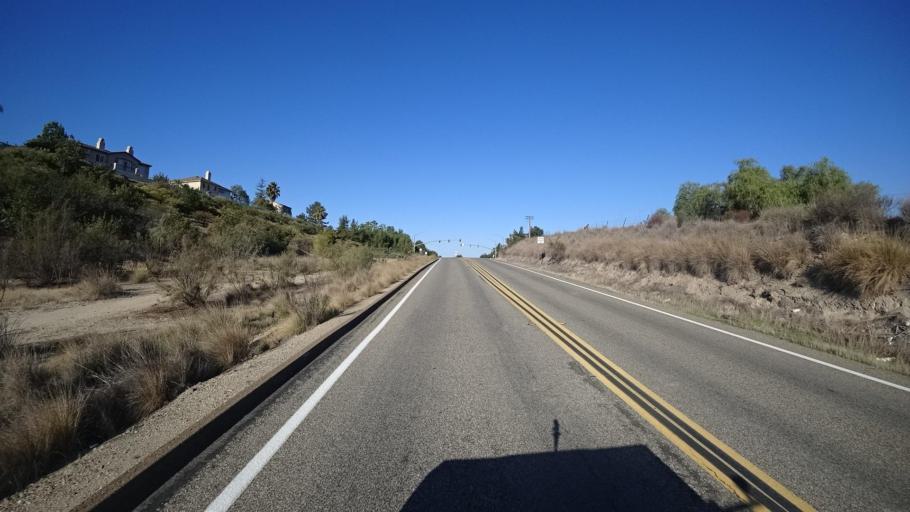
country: US
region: California
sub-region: San Diego County
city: La Presa
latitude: 32.6436
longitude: -116.9377
